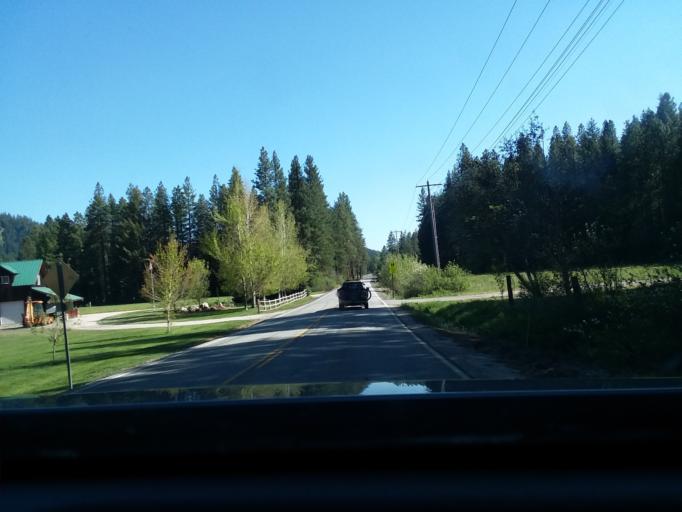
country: US
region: Washington
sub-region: Chelan County
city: Leavenworth
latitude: 47.7732
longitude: -120.6674
